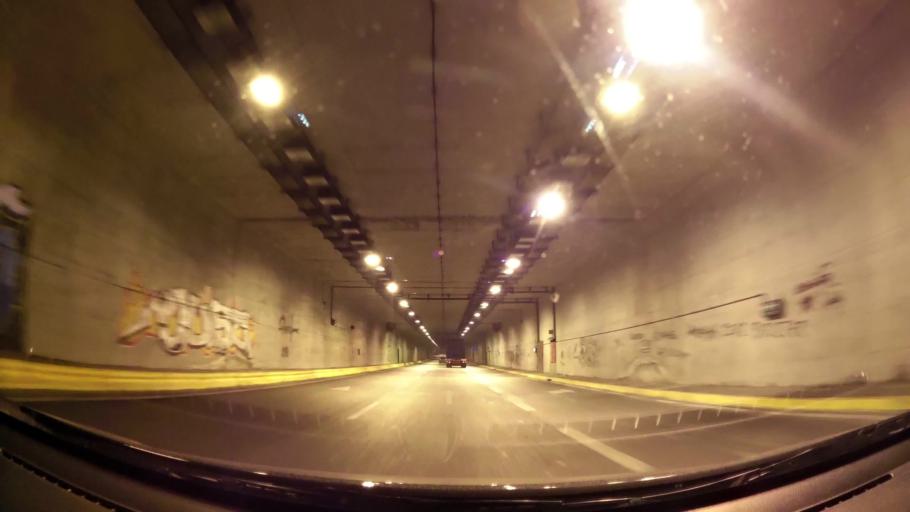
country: GR
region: Attica
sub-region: Nomos Piraios
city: Drapetsona
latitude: 37.9447
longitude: 23.6204
